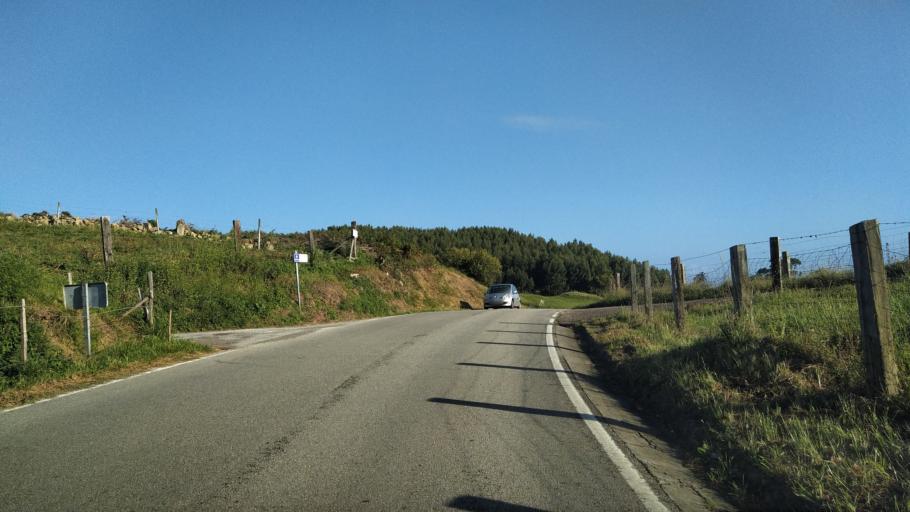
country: ES
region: Cantabria
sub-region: Provincia de Cantabria
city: Santa Cruz de Bezana
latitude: 43.4524
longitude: -3.9284
